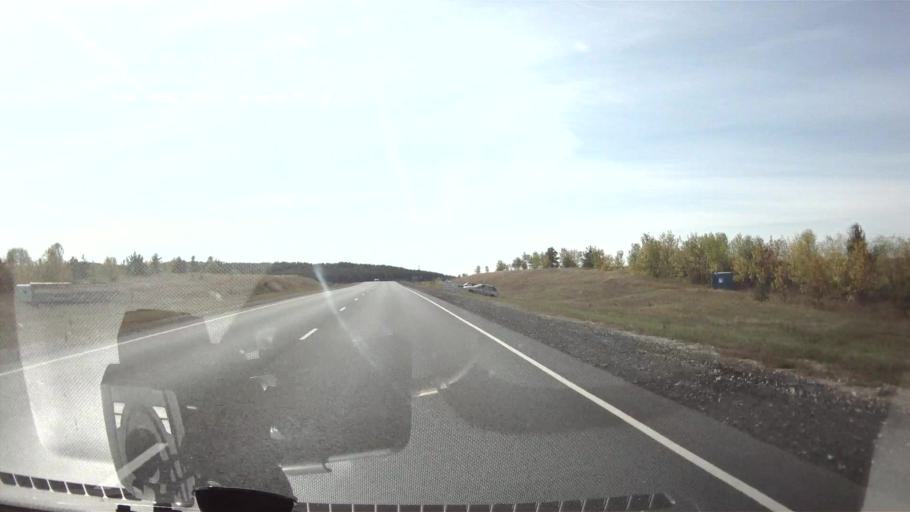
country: RU
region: Saratov
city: Khvalynsk
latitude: 52.5502
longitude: 48.0735
